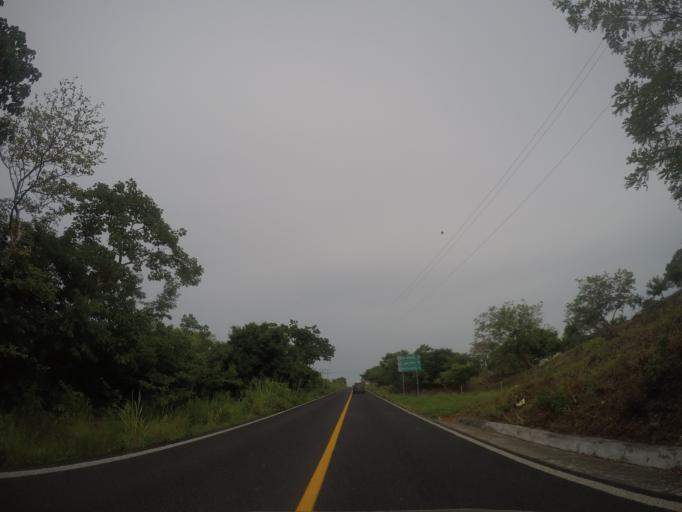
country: MX
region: Oaxaca
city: San Pedro Mixtepec
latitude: 15.9502
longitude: -97.2803
